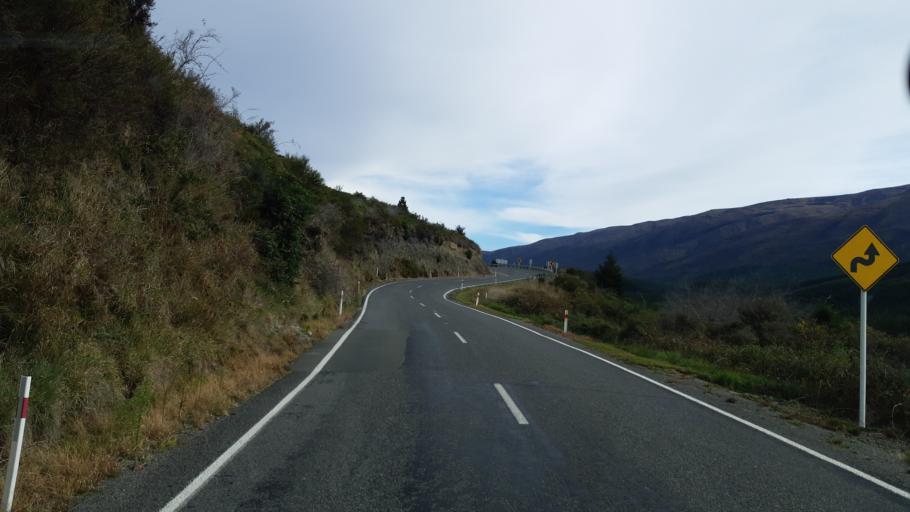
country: NZ
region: Tasman
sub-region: Tasman District
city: Wakefield
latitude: -41.6959
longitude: 173.1358
